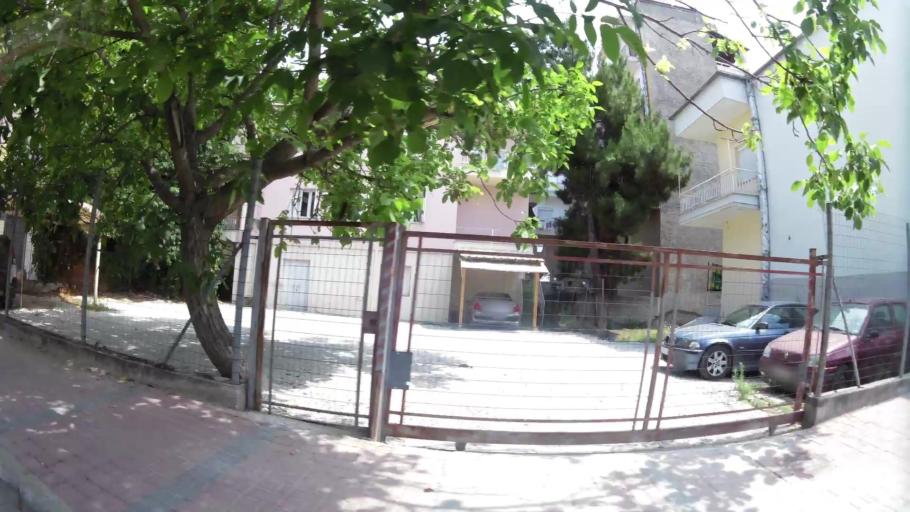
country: GR
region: Central Macedonia
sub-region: Nomos Pierias
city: Katerini
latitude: 40.2691
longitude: 22.5087
